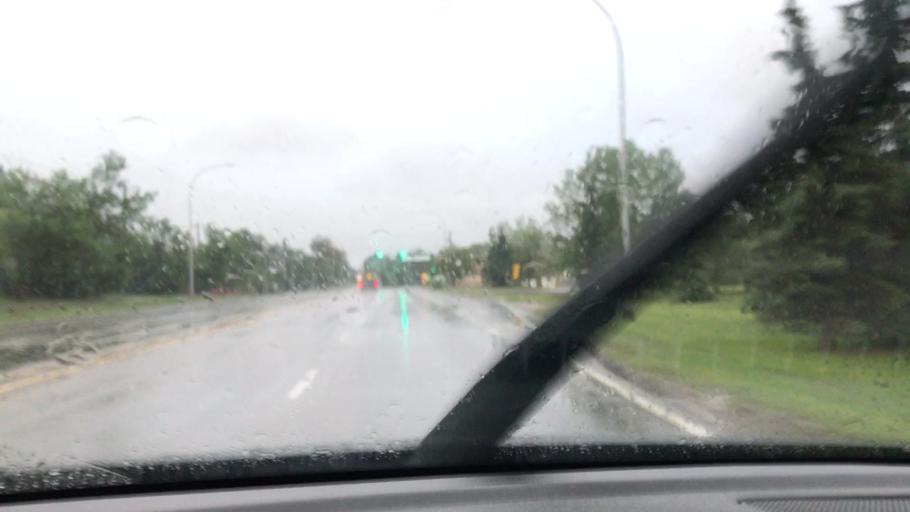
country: CA
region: Alberta
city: Sherwood Park
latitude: 53.5212
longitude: -113.3167
